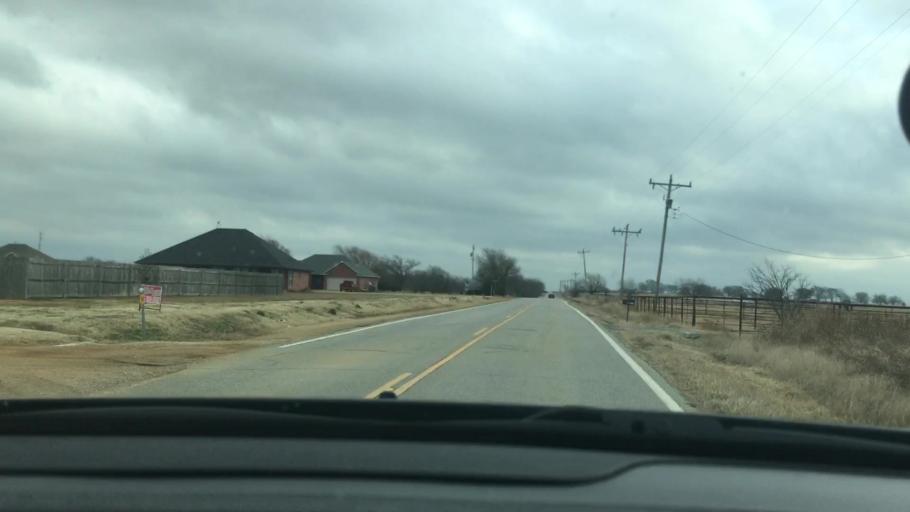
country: US
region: Oklahoma
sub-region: Bryan County
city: Durant
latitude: 34.0848
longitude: -96.4235
